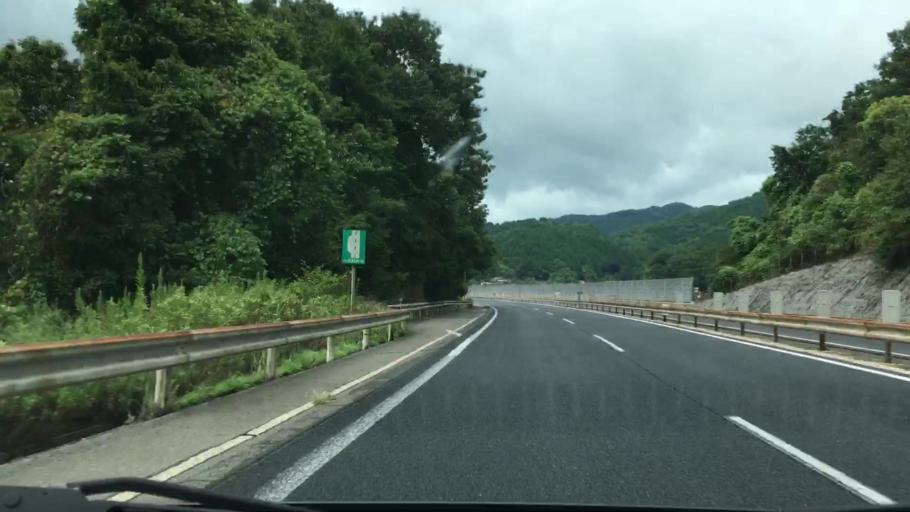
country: JP
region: Okayama
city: Takahashi
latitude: 34.9890
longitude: 133.7022
